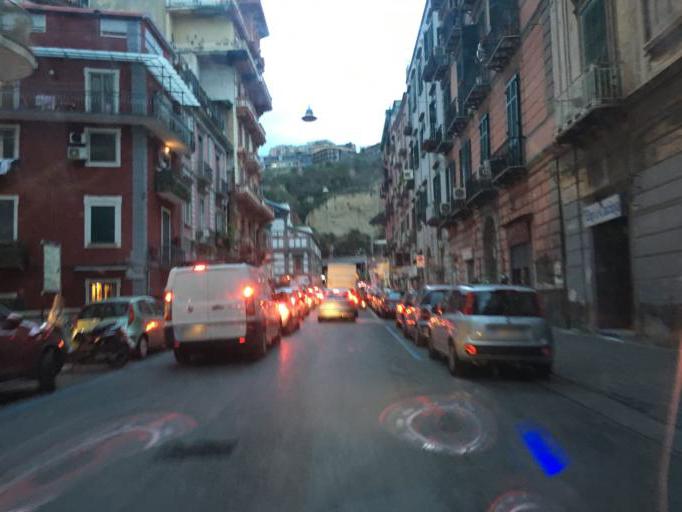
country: IT
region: Campania
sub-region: Provincia di Napoli
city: Napoli
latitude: 40.8312
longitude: 14.2209
